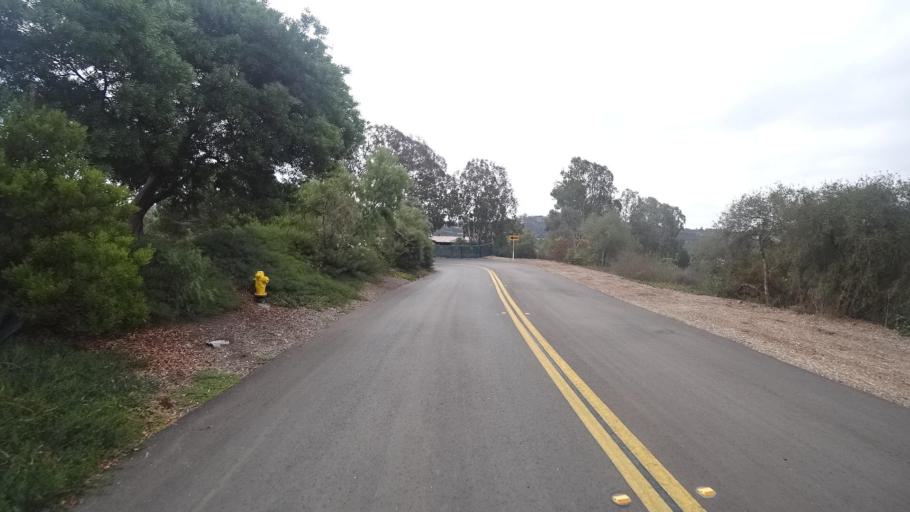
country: US
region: California
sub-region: San Diego County
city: Rancho Santa Fe
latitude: 33.0162
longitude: -117.2354
